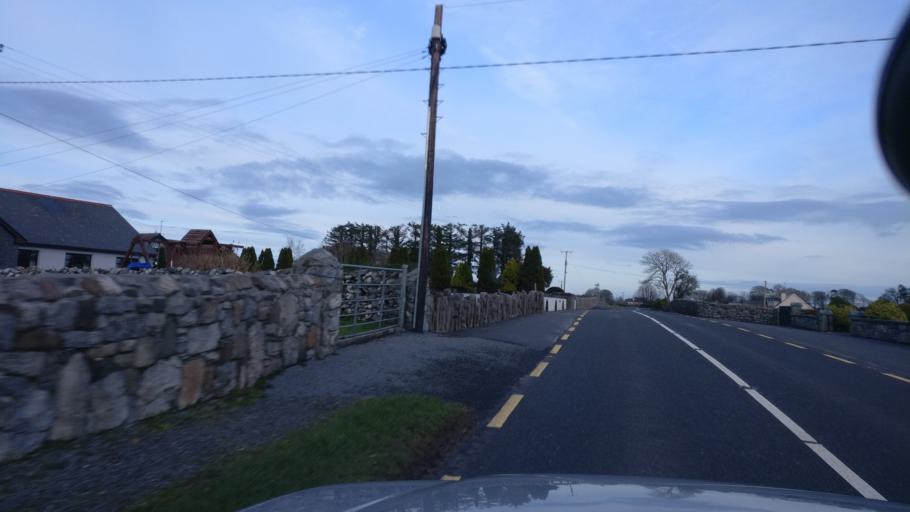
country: IE
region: Connaught
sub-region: Maigh Eo
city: Ballinrobe
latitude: 53.5407
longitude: -9.2553
